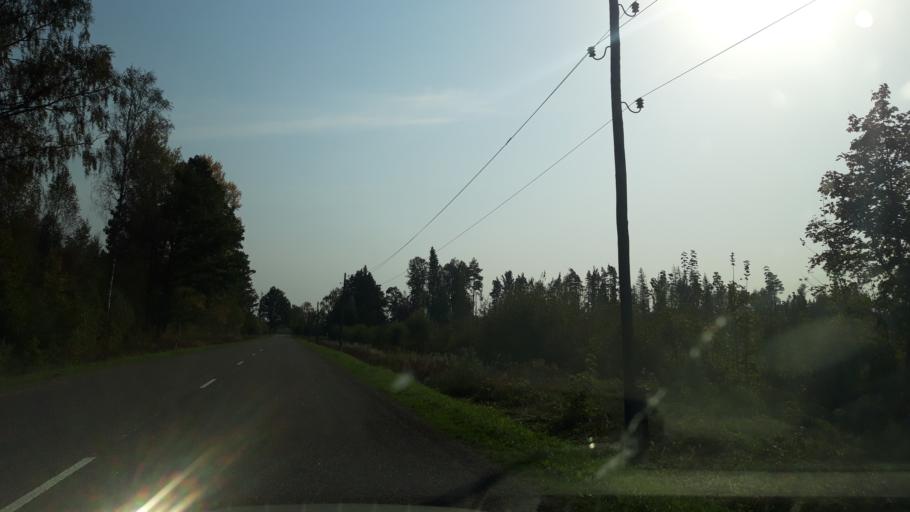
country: LV
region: Burtnieki
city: Matisi
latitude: 57.6293
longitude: 25.2645
